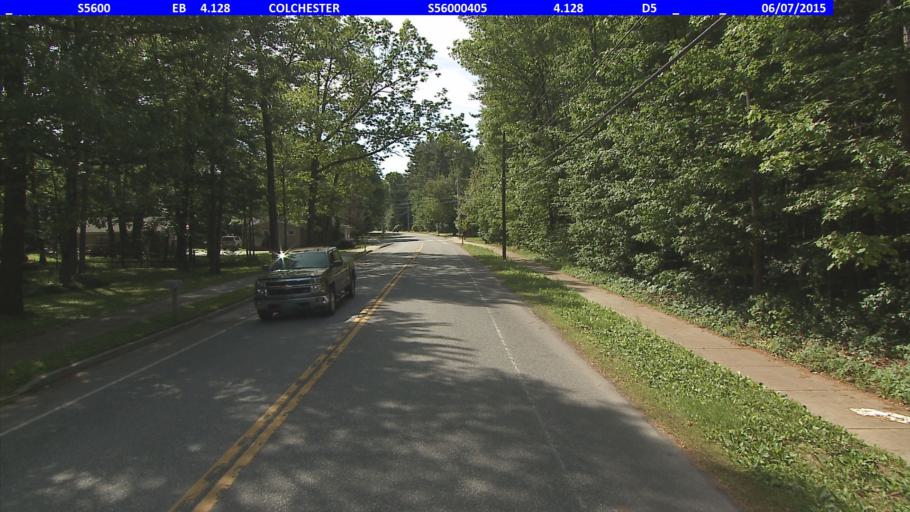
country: US
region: Vermont
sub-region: Chittenden County
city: Winooski
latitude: 44.5340
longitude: -73.2043
